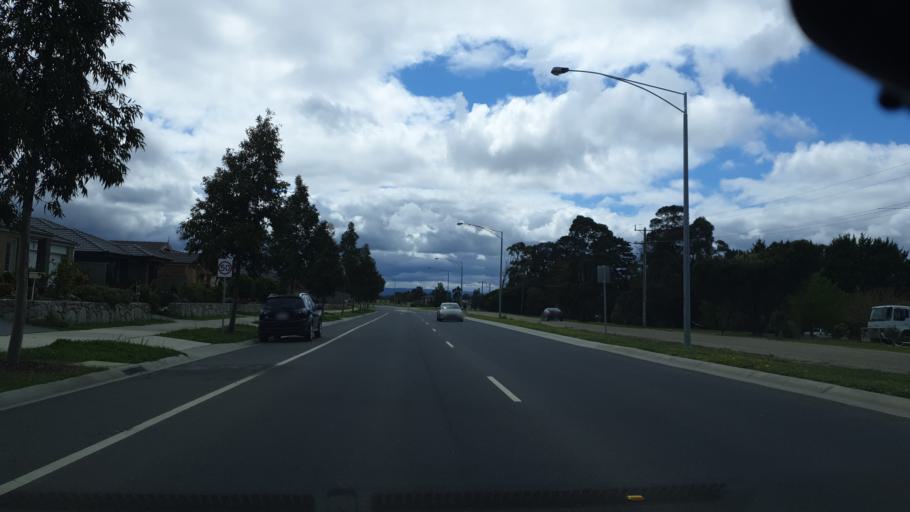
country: AU
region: Victoria
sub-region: Casey
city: Cranbourne East
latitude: -38.1052
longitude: 145.3108
